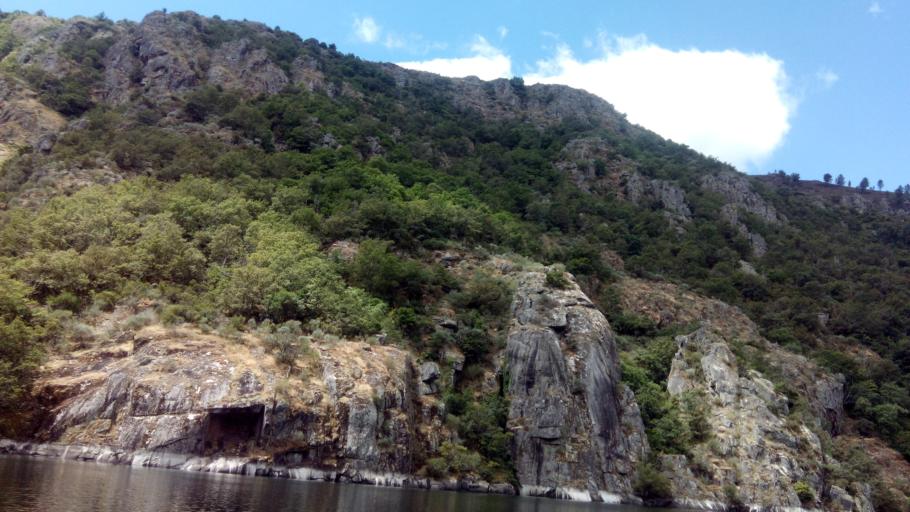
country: ES
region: Galicia
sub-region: Provincia de Lugo
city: Sober
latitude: 42.3941
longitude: -7.6256
